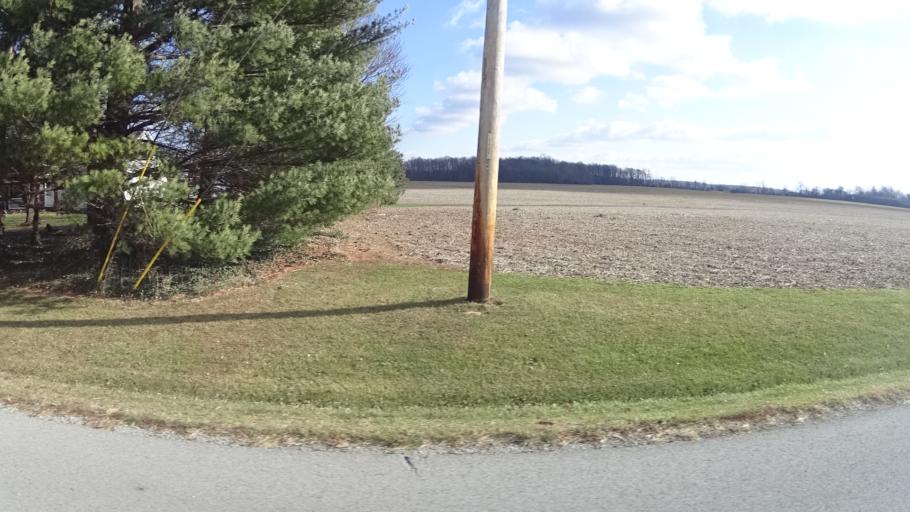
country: US
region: Ohio
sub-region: Lorain County
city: Camden
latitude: 41.2655
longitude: -82.2891
